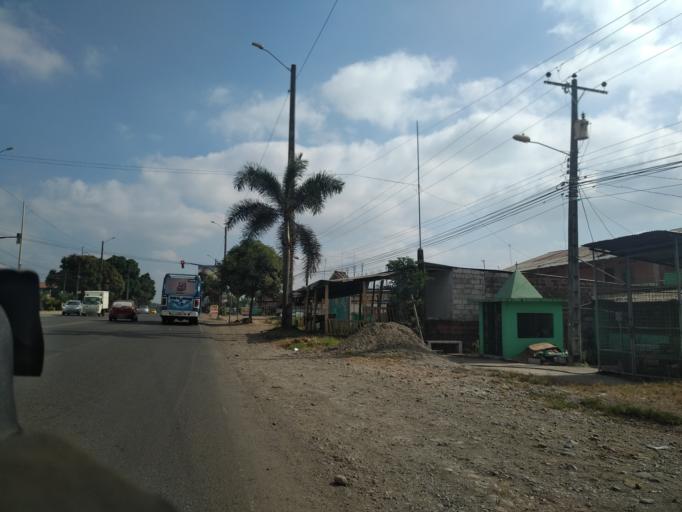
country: EC
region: Los Rios
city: Quevedo
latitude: -1.0585
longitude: -79.4884
